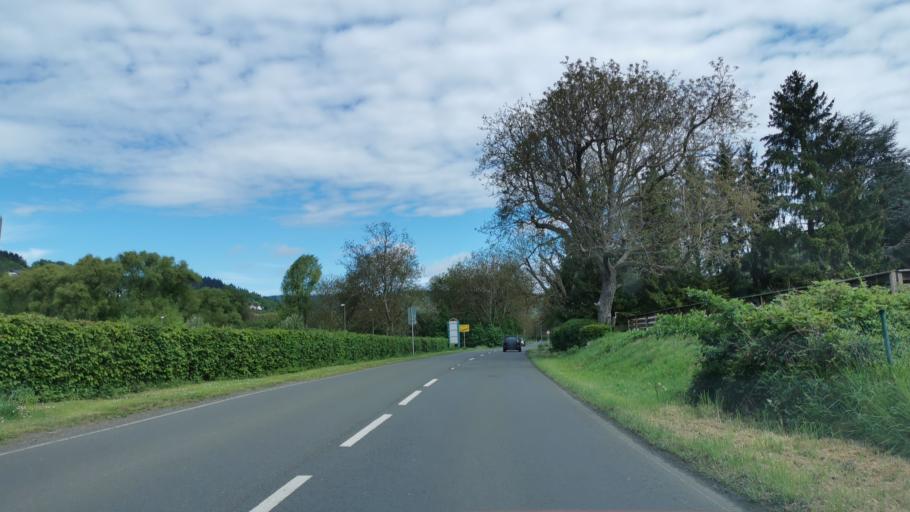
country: DE
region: Rheinland-Pfalz
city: Traben-Trarbach
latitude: 49.9577
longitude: 7.1048
